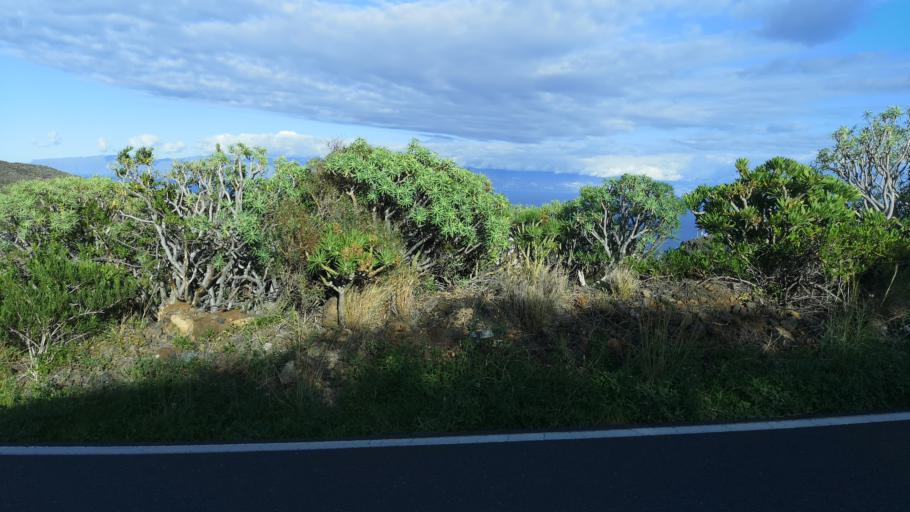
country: ES
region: Canary Islands
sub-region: Provincia de Santa Cruz de Tenerife
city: San Sebastian de la Gomera
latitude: 28.0850
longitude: -17.1340
